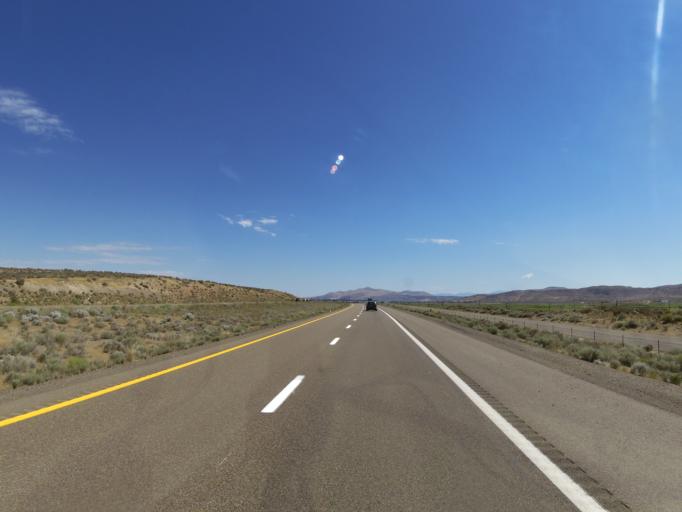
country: US
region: Nevada
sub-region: Elko County
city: Elko
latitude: 40.7919
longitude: -115.8530
